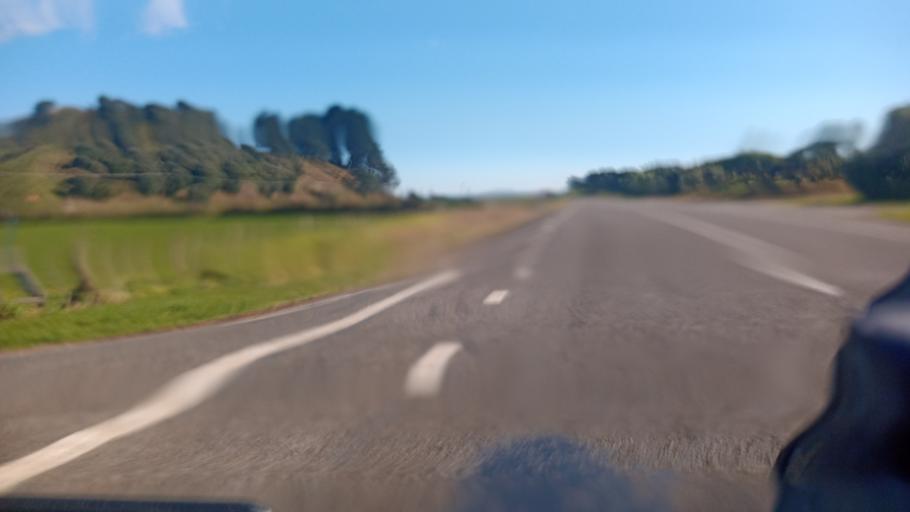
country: NZ
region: Bay of Plenty
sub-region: Opotiki District
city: Opotiki
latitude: -37.9909
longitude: 177.3121
